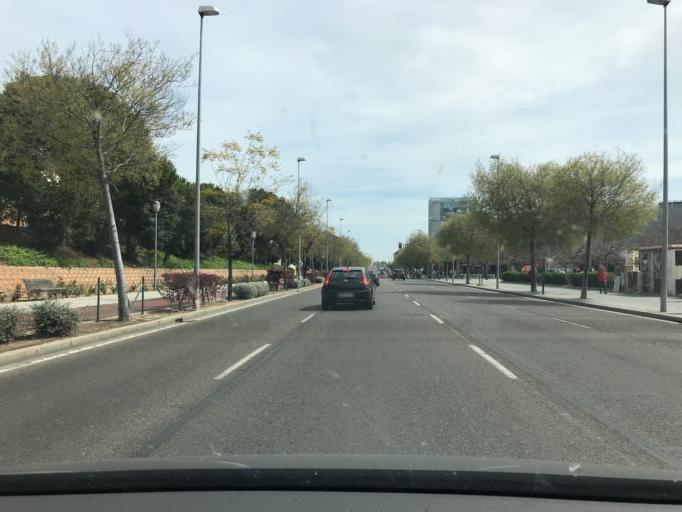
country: ES
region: Andalusia
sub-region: Province of Cordoba
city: Cordoba
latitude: 37.8938
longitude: -4.7774
